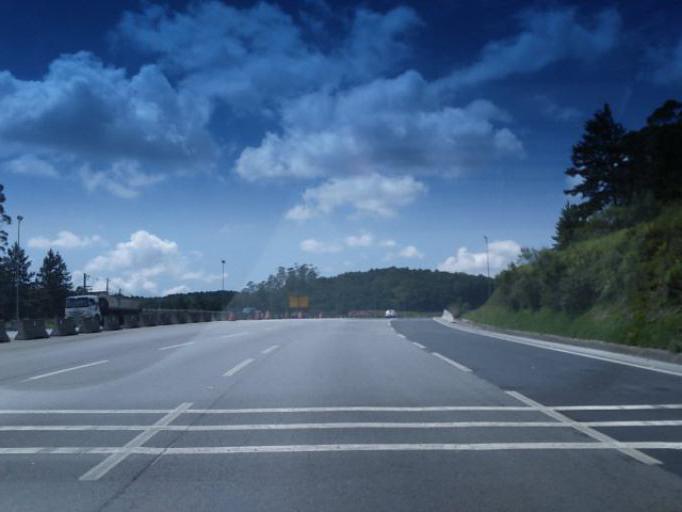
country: BR
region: Sao Paulo
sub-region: Sao Lourenco Da Serra
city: Sao Lourenco da Serra
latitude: -23.7845
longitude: -46.9141
